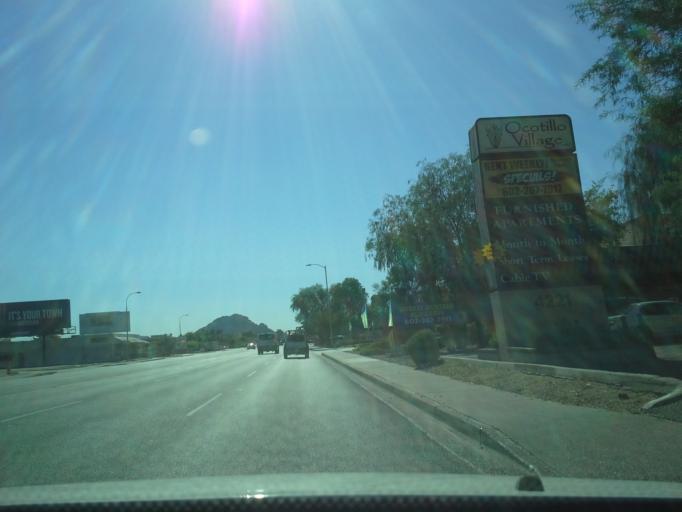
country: US
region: Arizona
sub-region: Maricopa County
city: Tempe Junction
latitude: 33.4656
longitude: -111.9907
